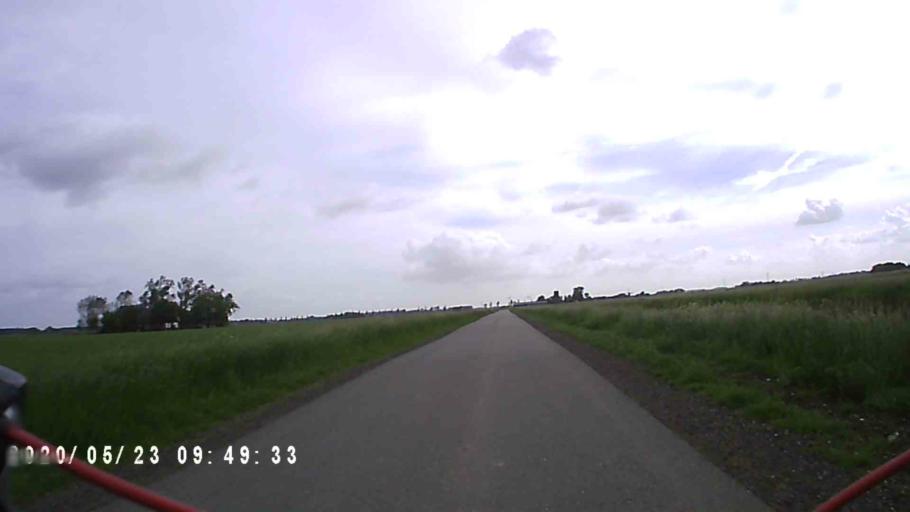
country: NL
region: Groningen
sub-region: Gemeente Slochteren
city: Slochteren
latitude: 53.2928
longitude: 6.7657
